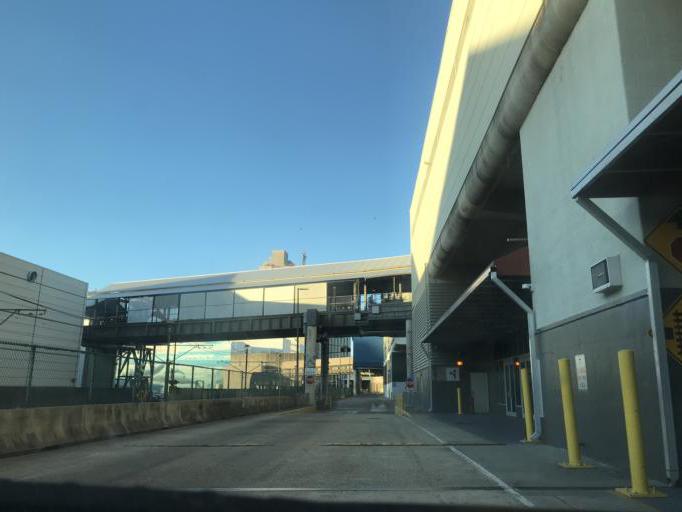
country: US
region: Louisiana
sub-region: Orleans Parish
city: New Orleans
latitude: 29.9433
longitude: -90.0622
